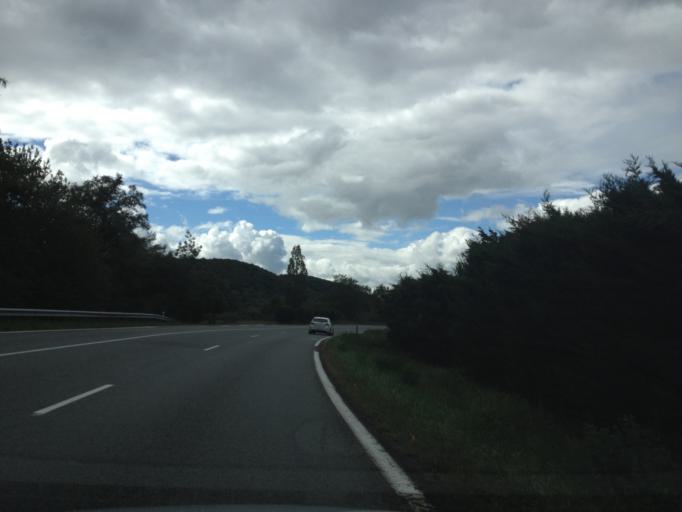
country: FR
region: Rhone-Alpes
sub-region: Departement de la Loire
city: Saint-Symphorien-de-Lay
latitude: 45.9629
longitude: 4.1734
